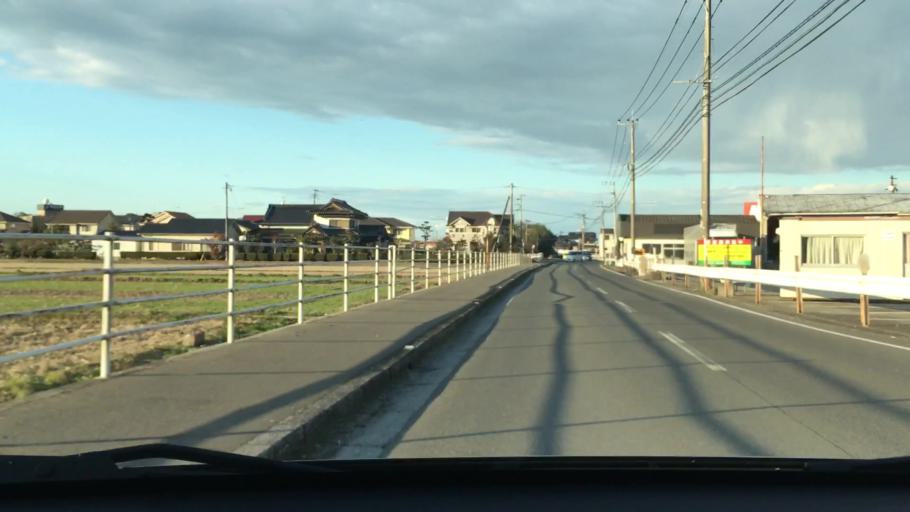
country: JP
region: Oita
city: Bungo-Takada-shi
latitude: 33.5200
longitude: 131.3481
